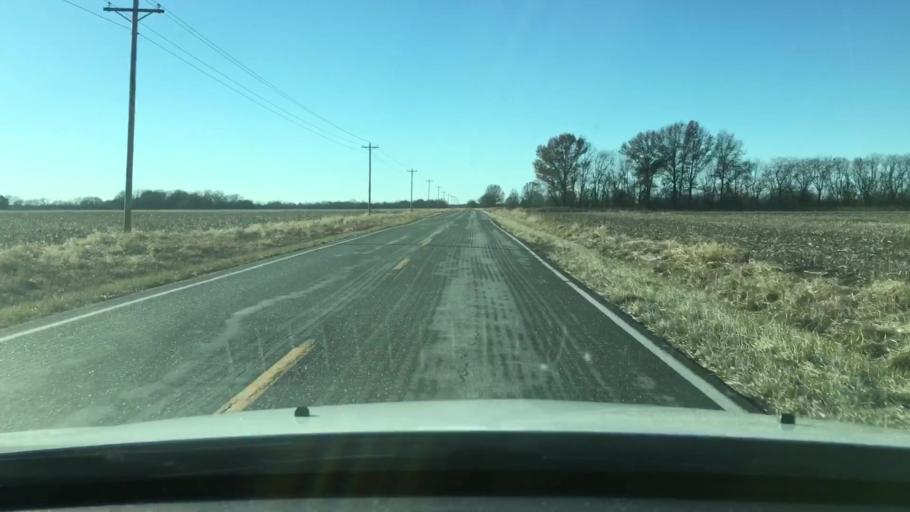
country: US
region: Missouri
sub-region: Audrain County
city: Mexico
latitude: 39.2809
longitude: -91.7463
